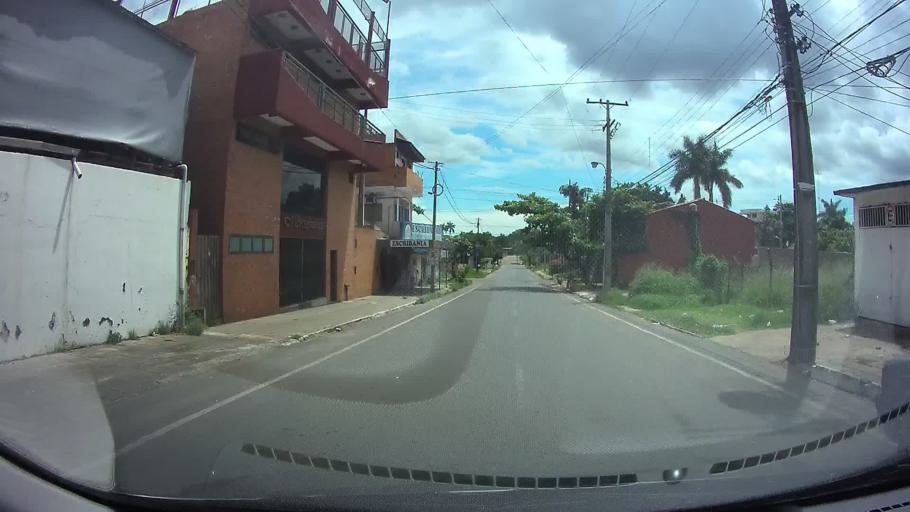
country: PY
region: Central
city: Fernando de la Mora
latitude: -25.3170
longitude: -57.5264
